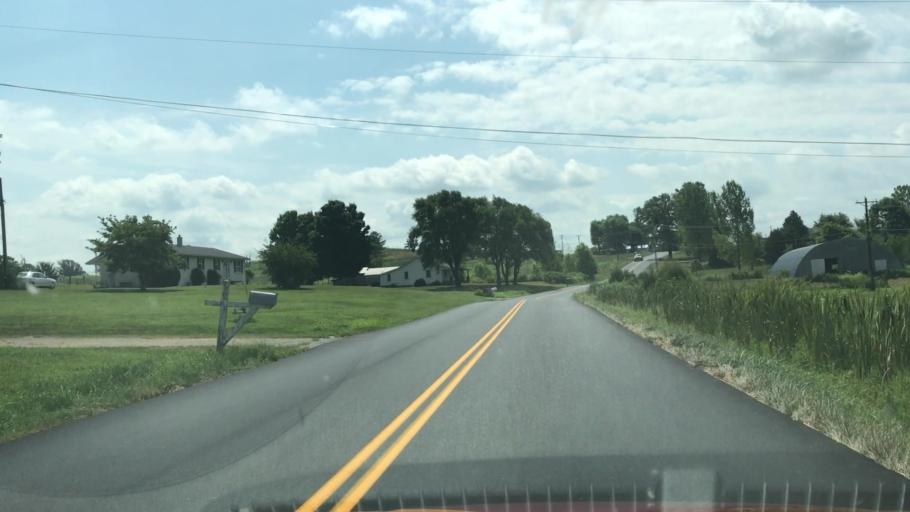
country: US
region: Kentucky
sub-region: Monroe County
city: Tompkinsville
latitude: 36.7345
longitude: -85.7338
